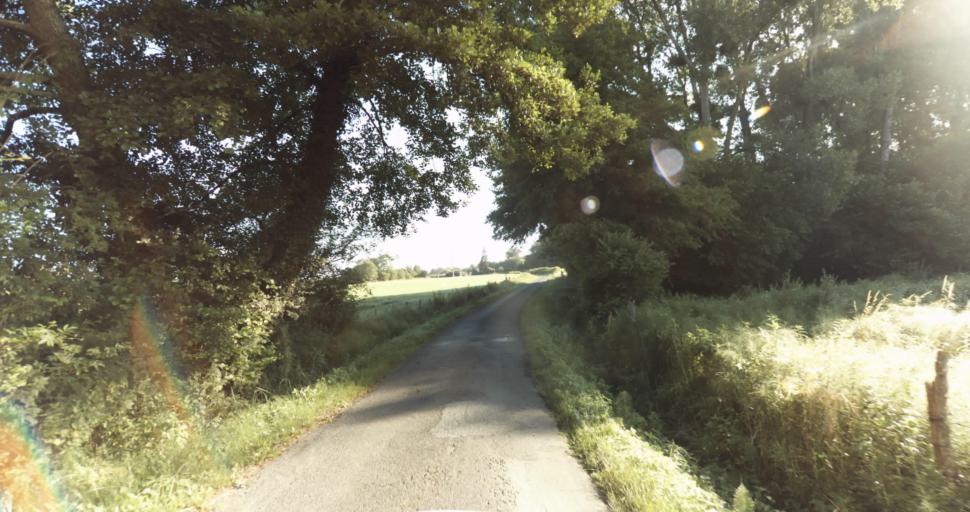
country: FR
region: Aquitaine
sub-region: Departement de la Gironde
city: Bazas
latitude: 44.4058
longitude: -0.2133
